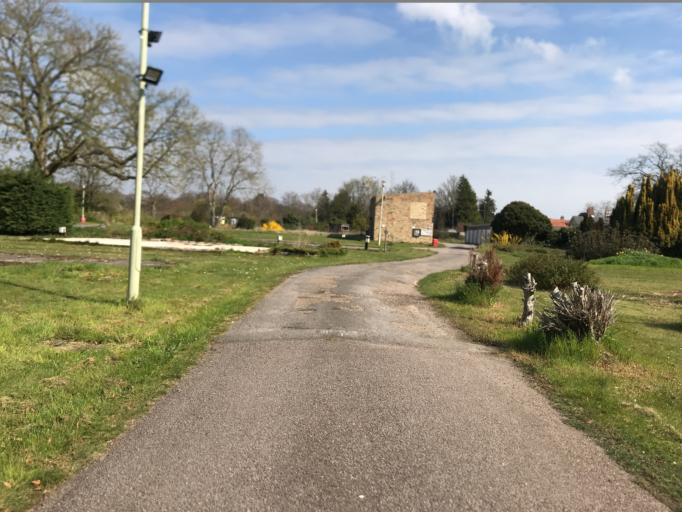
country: GB
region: England
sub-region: Cambridgeshire
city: Sawston
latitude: 52.1520
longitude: 0.1428
